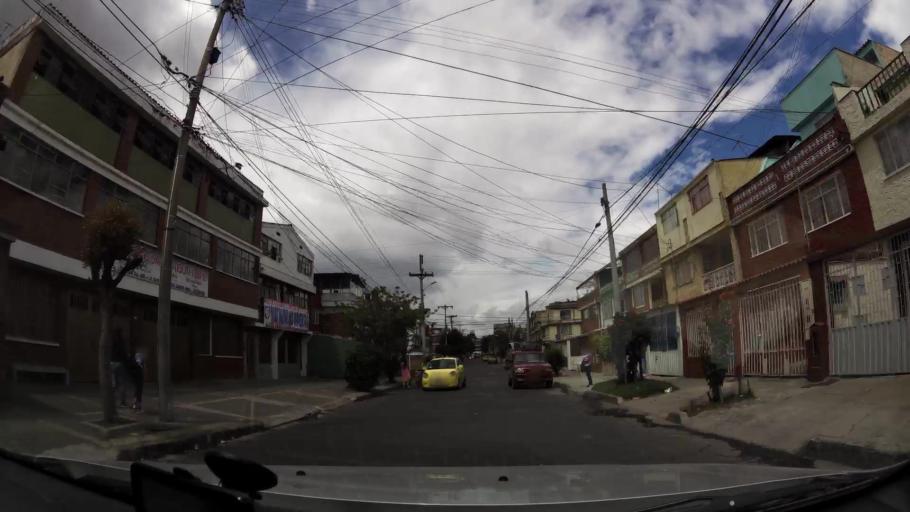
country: CO
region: Bogota D.C.
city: Bogota
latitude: 4.5993
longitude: -74.1215
